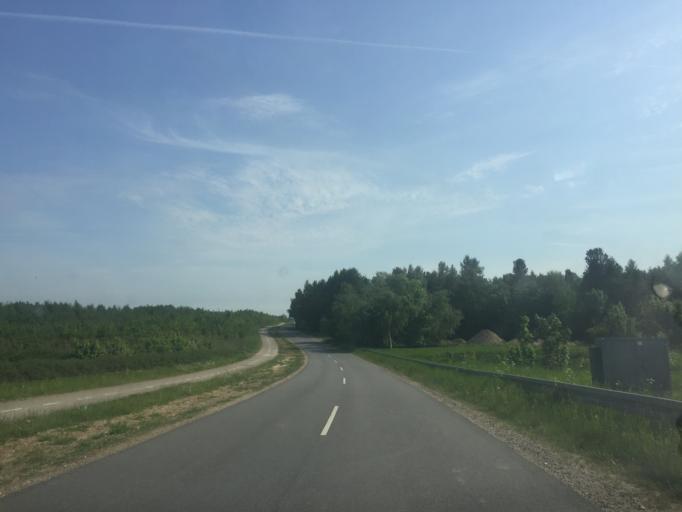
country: DK
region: Capital Region
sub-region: Egedal Kommune
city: Smorumnedre
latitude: 55.7259
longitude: 12.2908
